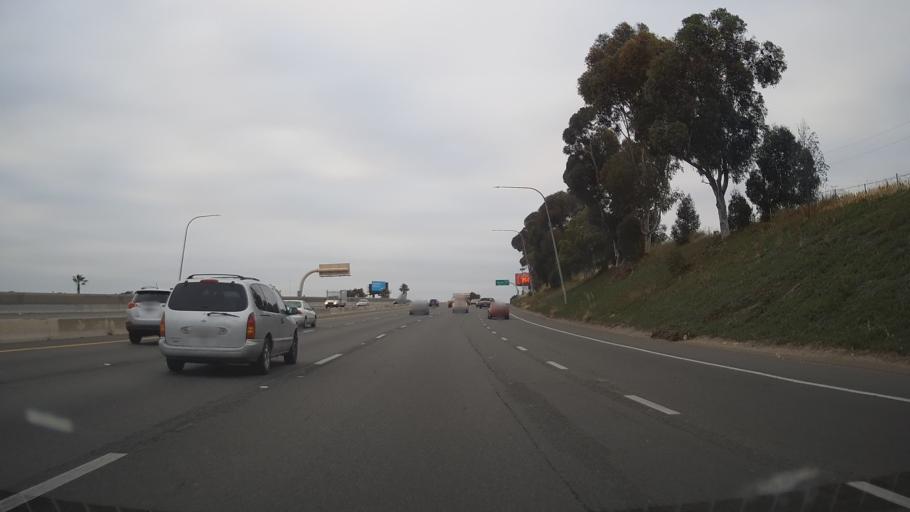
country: US
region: California
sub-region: San Diego County
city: National City
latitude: 32.7038
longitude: -117.1206
